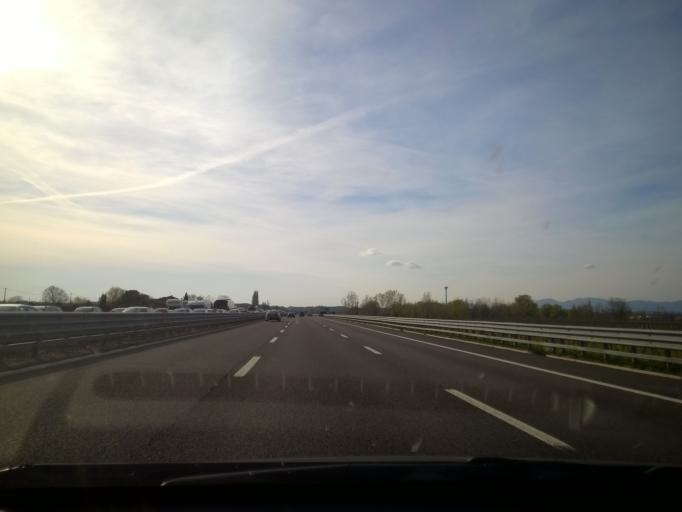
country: IT
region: Lombardy
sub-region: Provincia di Brescia
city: San Martino della Battaglia
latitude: 45.4385
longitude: 10.5779
